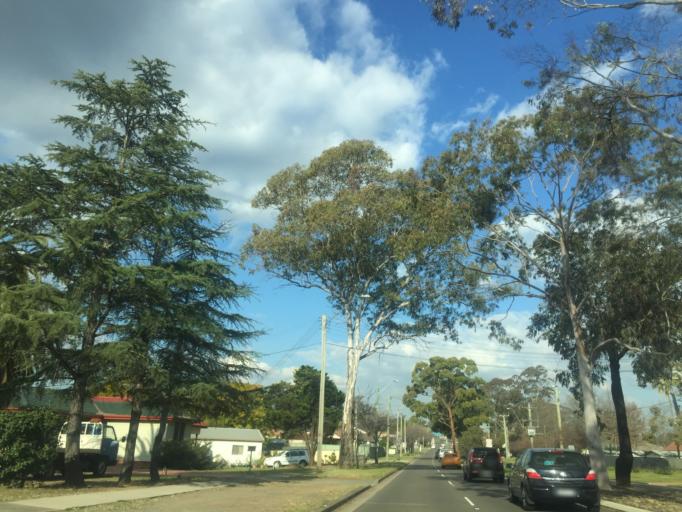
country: AU
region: New South Wales
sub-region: Blacktown
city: Quakers Hill
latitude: -33.7535
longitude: 150.8893
